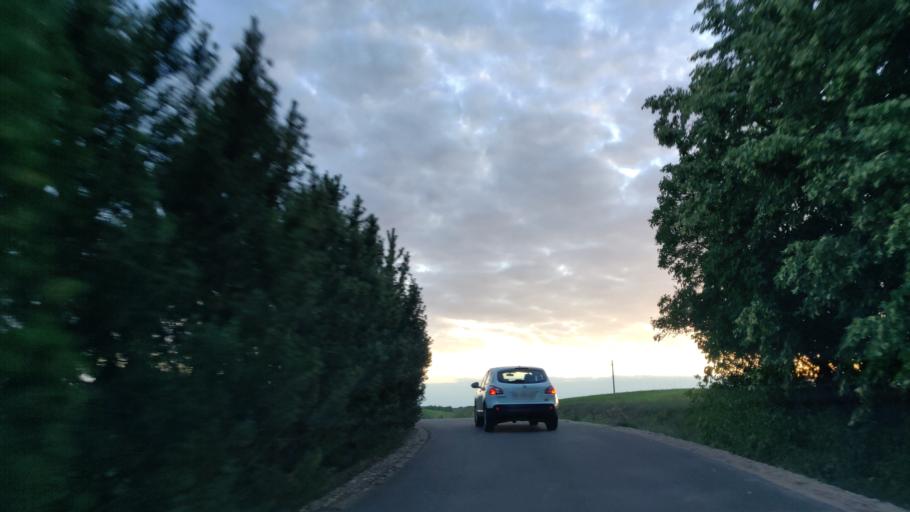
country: LT
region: Vilnius County
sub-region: Trakai
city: Rudiskes
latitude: 54.6087
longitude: 24.8108
